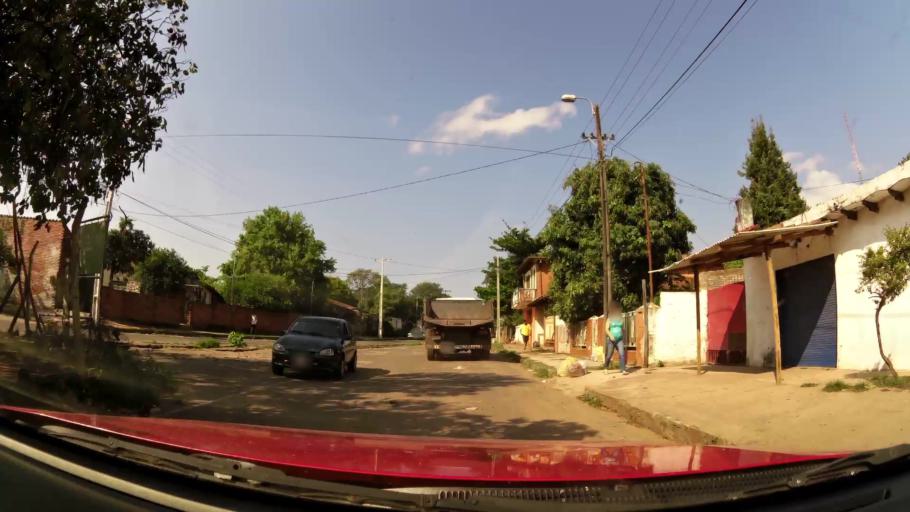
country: PY
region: Asuncion
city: Asuncion
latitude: -25.3205
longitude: -57.6403
